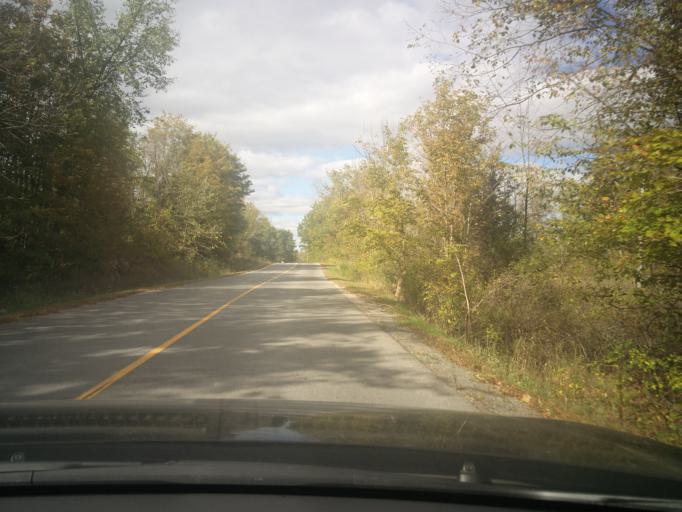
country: CA
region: Ontario
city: Perth
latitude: 44.6493
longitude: -76.5394
